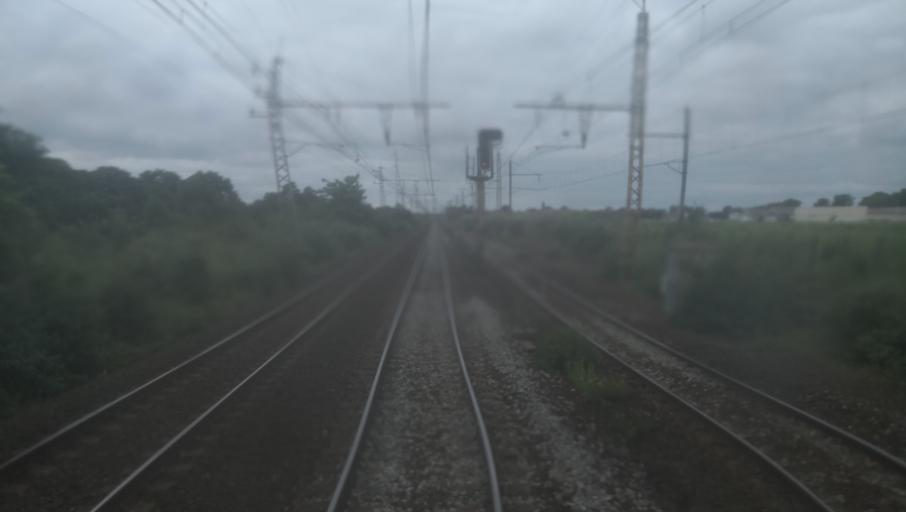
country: FR
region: Midi-Pyrenees
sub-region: Departement de la Haute-Garonne
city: Fenouillet
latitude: 43.6770
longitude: 1.4057
